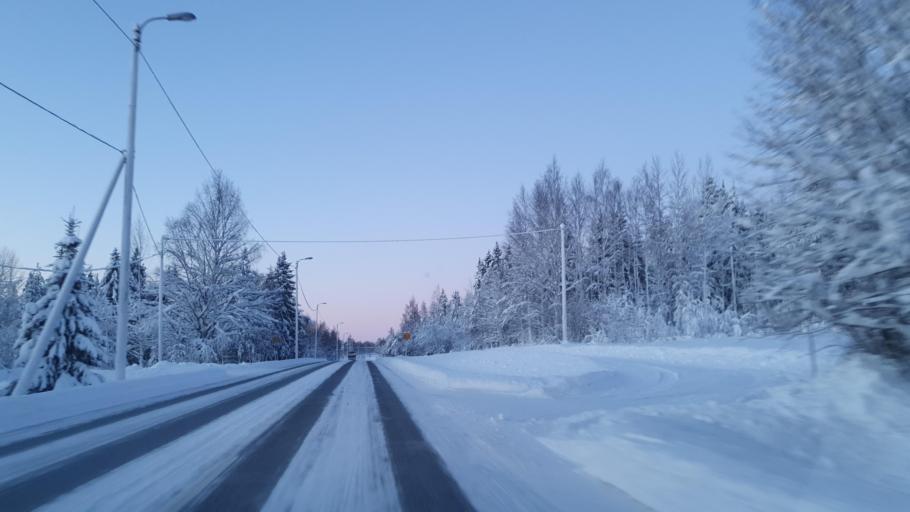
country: FI
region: Lapland
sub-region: Torniolaakso
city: Ylitornio
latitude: 66.2238
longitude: 23.7791
